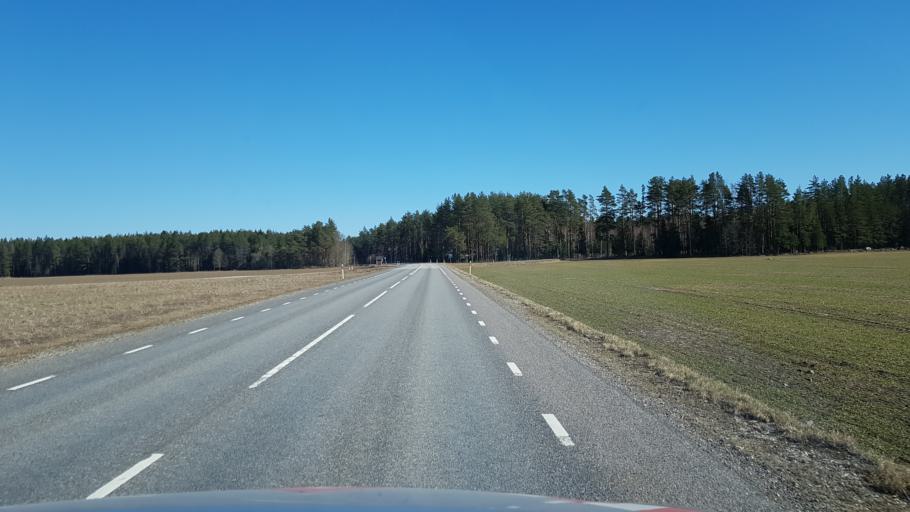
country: EE
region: Laeaene-Virumaa
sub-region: Viru-Nigula vald
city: Kunda
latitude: 59.3619
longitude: 26.6208
